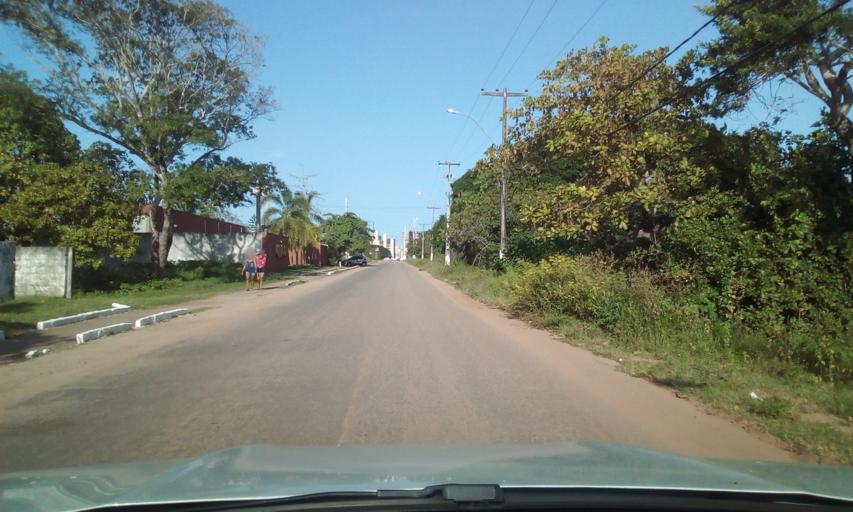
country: BR
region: Paraiba
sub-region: Cabedelo
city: Cabedelo
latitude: -7.0399
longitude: -34.8531
